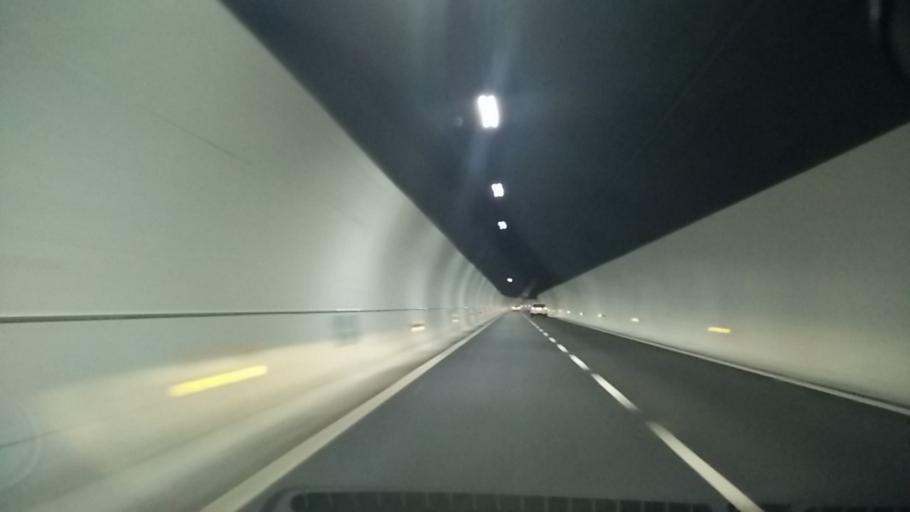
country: IT
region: Friuli Venezia Giulia
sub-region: Provincia di Udine
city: Chiusaforte
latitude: 46.4188
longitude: 13.3196
